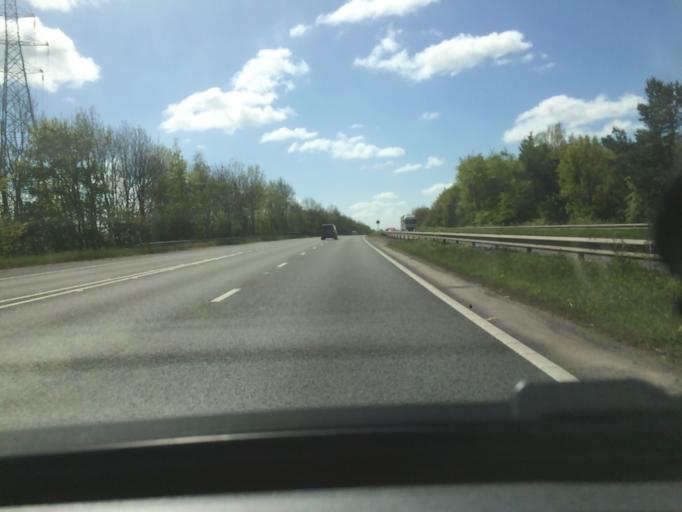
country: GB
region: Wales
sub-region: Wrexham
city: Rhosllanerchrugog
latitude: 53.0238
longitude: -3.0283
